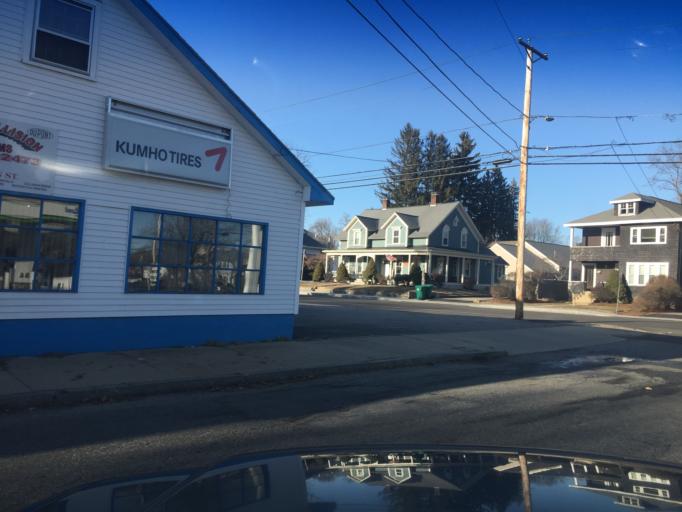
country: US
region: Massachusetts
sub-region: Worcester County
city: Uxbridge
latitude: 42.0812
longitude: -71.6371
